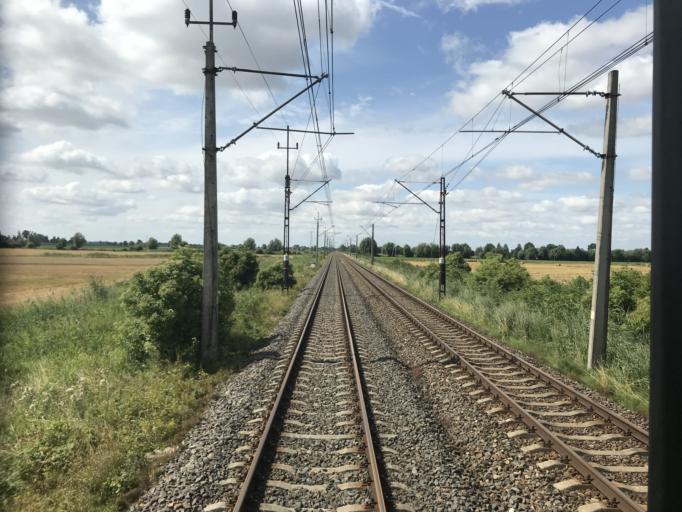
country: PL
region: Warmian-Masurian Voivodeship
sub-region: Powiat elblaski
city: Gronowo Elblaskie
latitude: 54.1138
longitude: 19.3471
